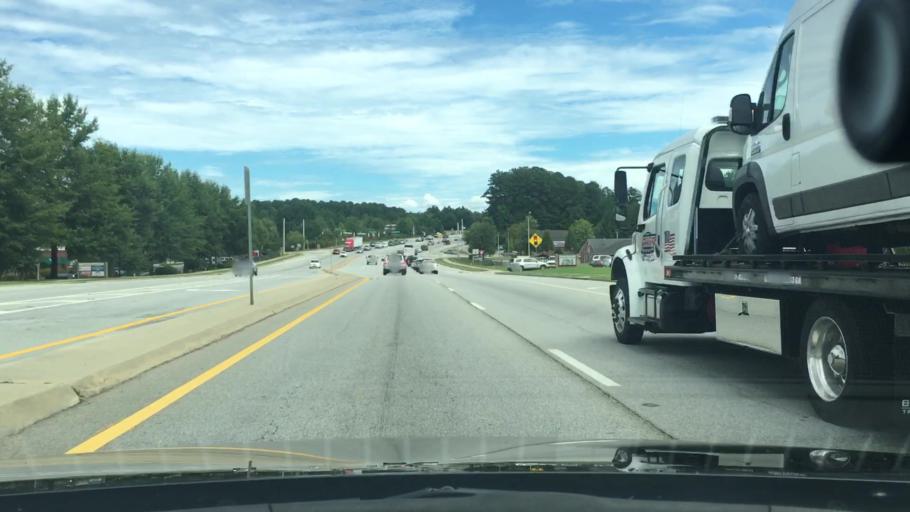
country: US
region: Georgia
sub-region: Coweta County
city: Newnan
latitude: 33.4006
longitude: -84.7732
